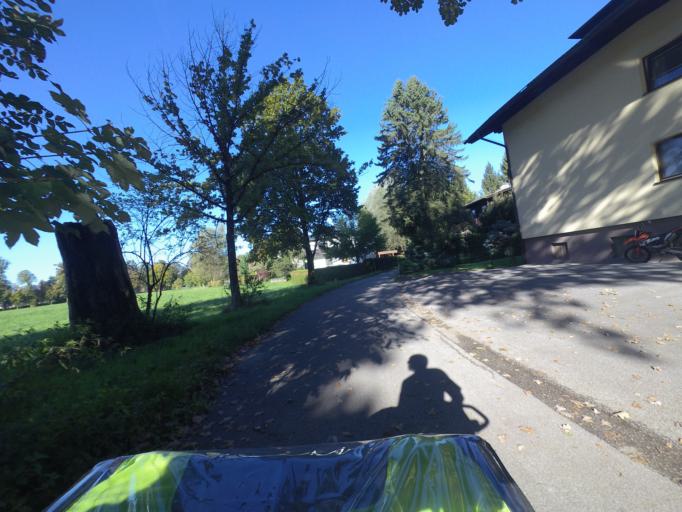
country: AT
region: Salzburg
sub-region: Salzburg Stadt
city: Salzburg
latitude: 47.7793
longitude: 13.0630
